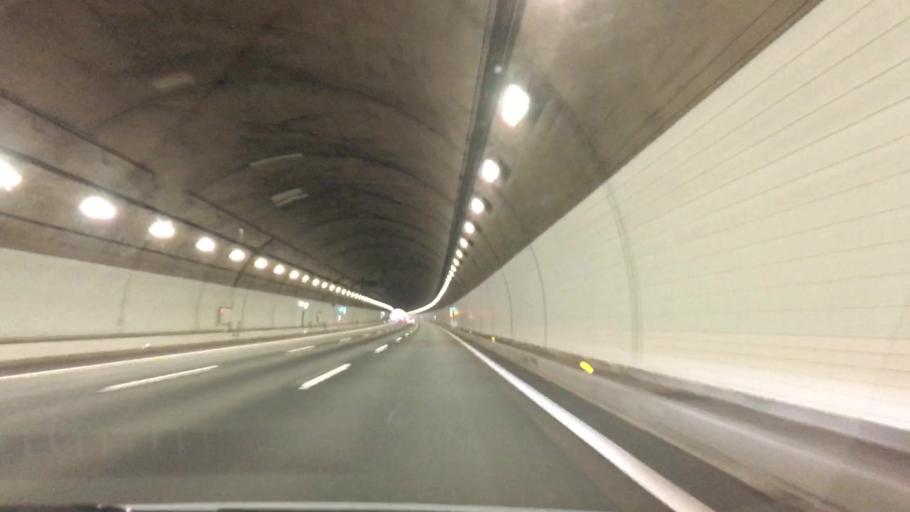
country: JP
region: Shizuoka
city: Kanaya
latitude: 34.8446
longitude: 138.0831
